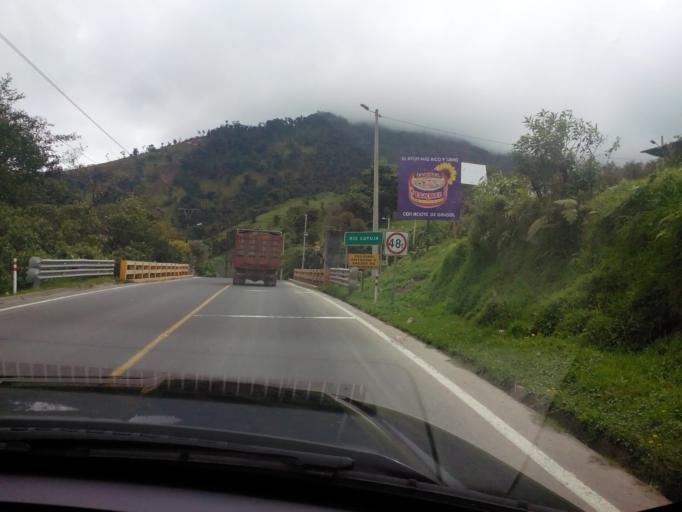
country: EC
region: Pichincha
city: Sangolqui
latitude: -0.4126
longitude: -78.0278
